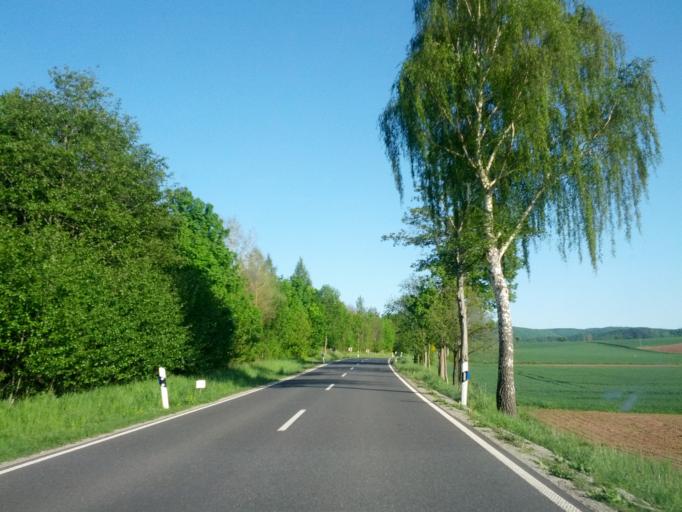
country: DE
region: Hesse
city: Wanfried
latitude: 51.1474
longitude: 10.1926
